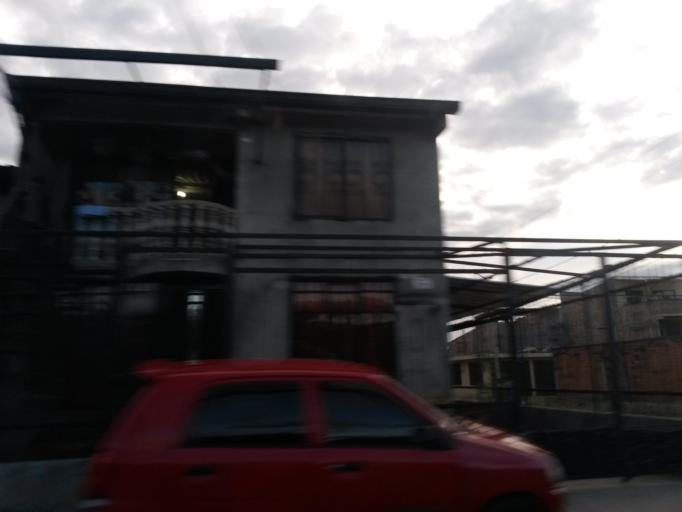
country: CO
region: Cauca
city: Popayan
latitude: 2.4598
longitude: -76.6364
